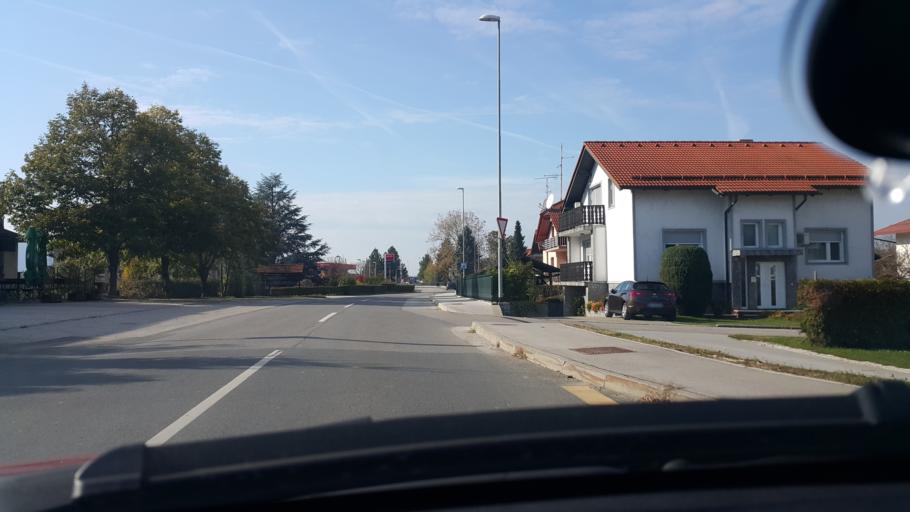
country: HR
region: Zagrebacka
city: Bregana
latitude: 45.8954
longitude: 15.6577
